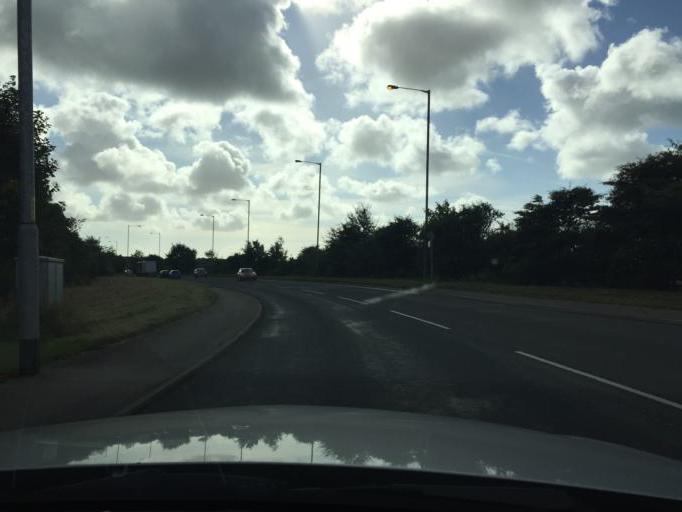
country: GB
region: England
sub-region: Lancashire
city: Kirkham
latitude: 53.7924
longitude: -2.8925
